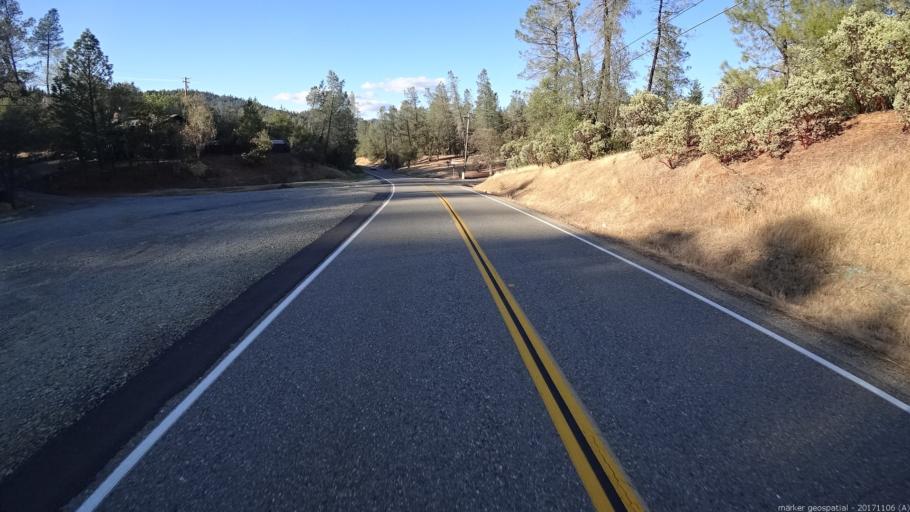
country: US
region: California
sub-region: Shasta County
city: Shasta
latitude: 40.5818
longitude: -122.4814
